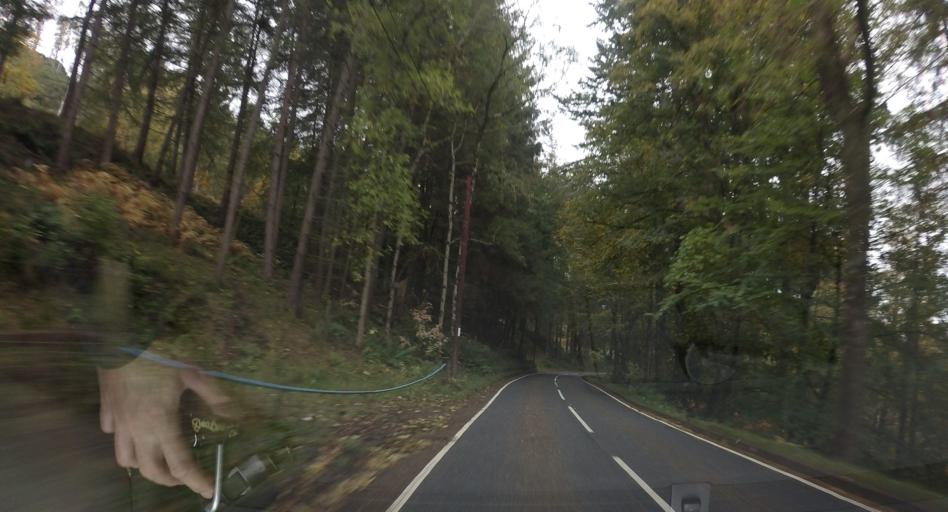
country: GB
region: Scotland
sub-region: Perth and Kinross
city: Bankfoot
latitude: 56.5571
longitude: -3.5602
